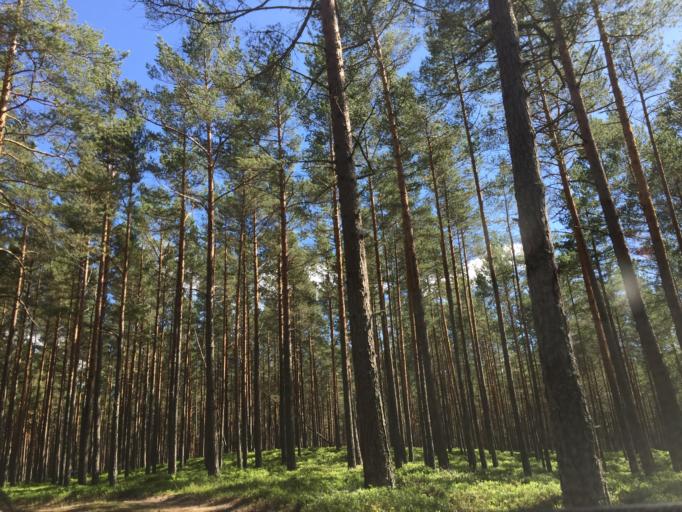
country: LV
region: Ventspils
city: Ventspils
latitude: 57.4737
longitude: 21.6463
